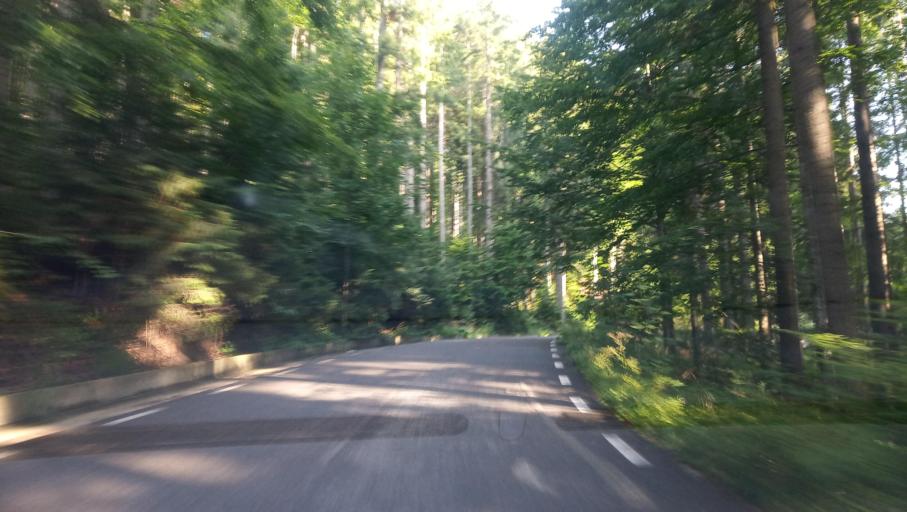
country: RO
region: Prahova
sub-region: Oras Sinaia
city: Sinaia
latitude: 45.3160
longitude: 25.5174
